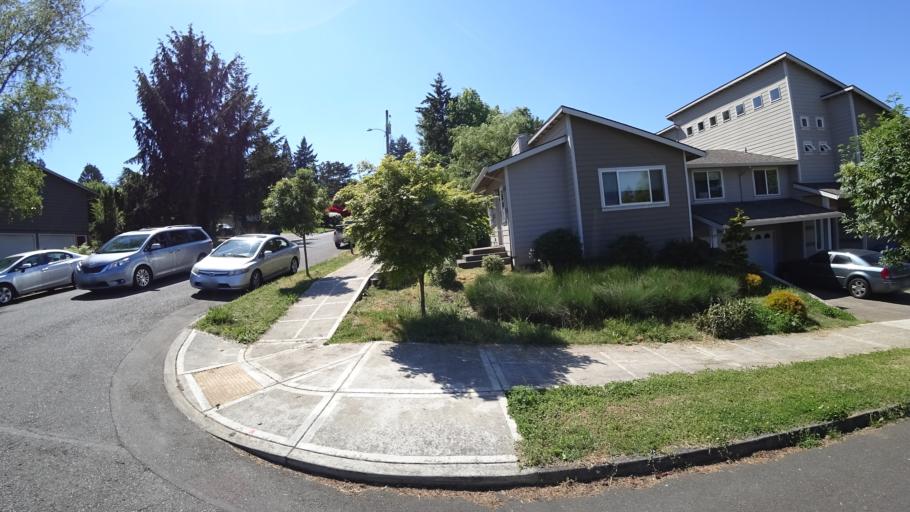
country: US
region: Oregon
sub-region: Washington County
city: Metzger
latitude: 45.4511
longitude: -122.7180
